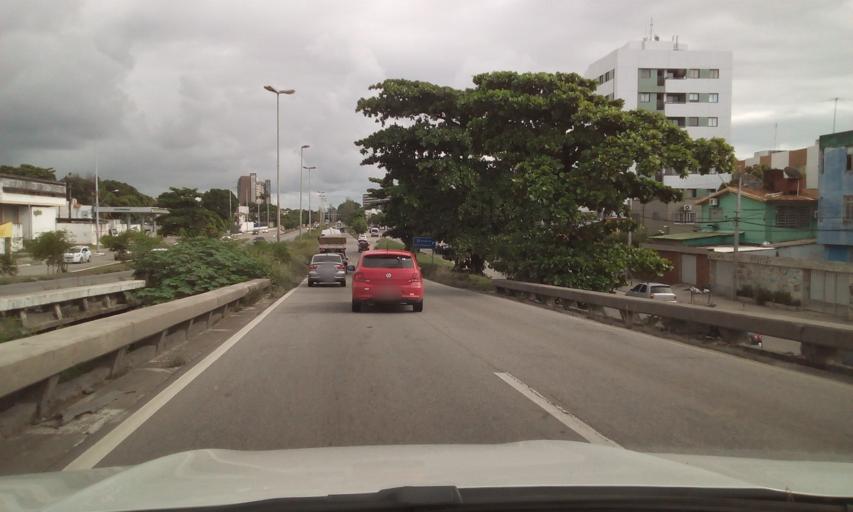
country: BR
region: Pernambuco
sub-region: Recife
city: Recife
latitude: -8.0400
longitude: -34.9423
